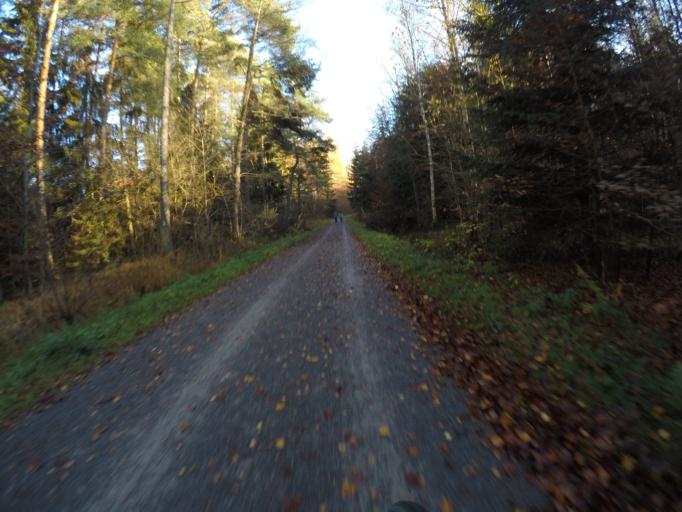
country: DE
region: Baden-Wuerttemberg
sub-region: Regierungsbezirk Stuttgart
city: Sindelfingen
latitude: 48.6943
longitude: 9.0508
